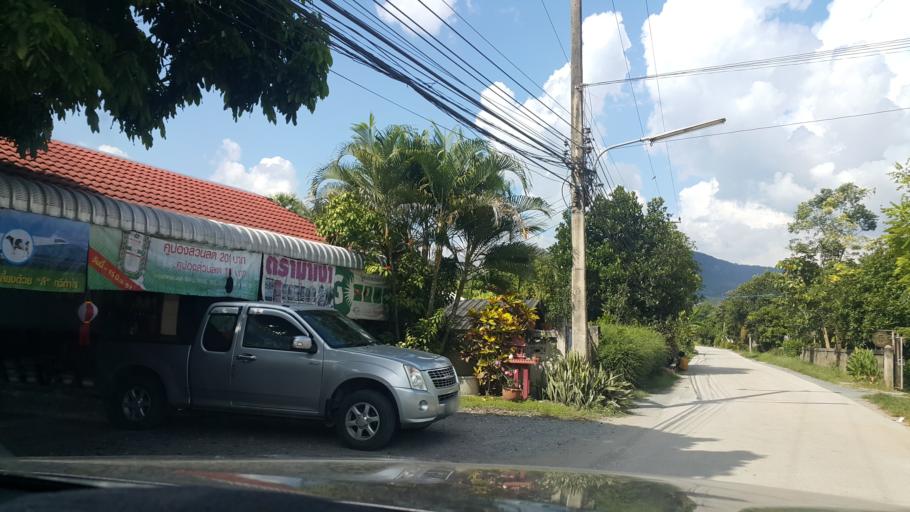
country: TH
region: Chiang Mai
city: Mae On
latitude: 18.7290
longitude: 99.2079
